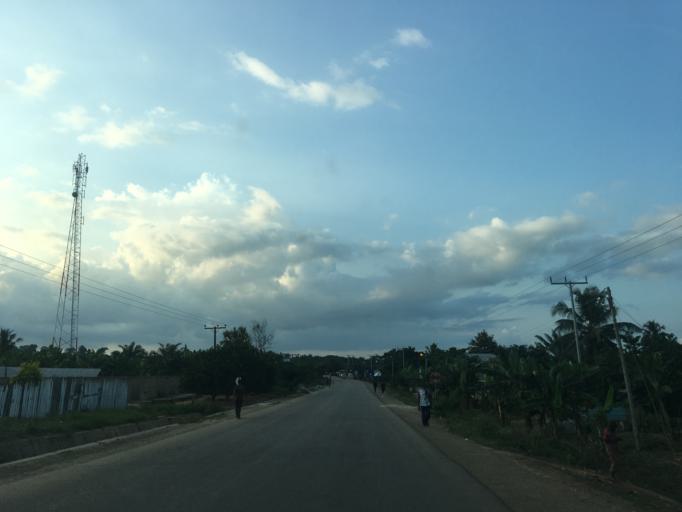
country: GH
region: Western
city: Bibiani
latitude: 6.6477
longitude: -2.4248
